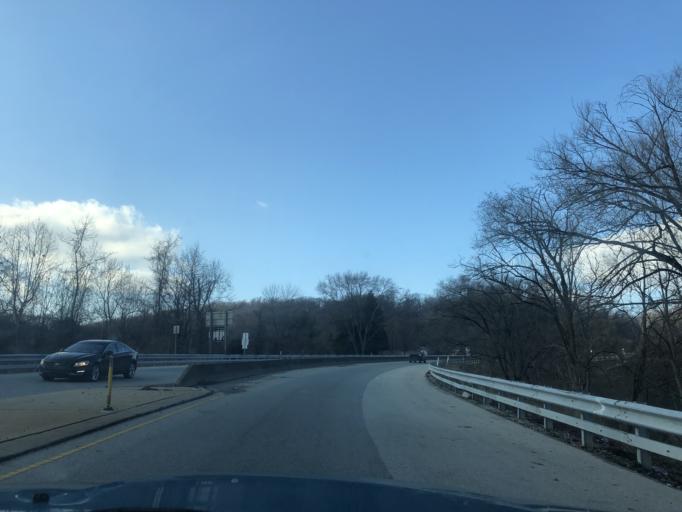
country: US
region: Pennsylvania
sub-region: Montgomery County
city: West Conshohocken
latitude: 40.0680
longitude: -75.3434
